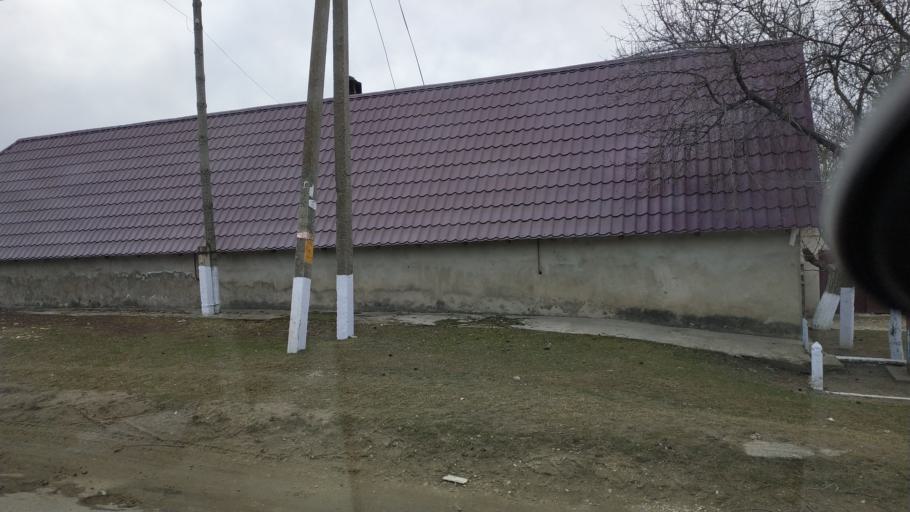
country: MD
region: Telenesti
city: Cocieri
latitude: 47.2689
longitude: 29.0661
